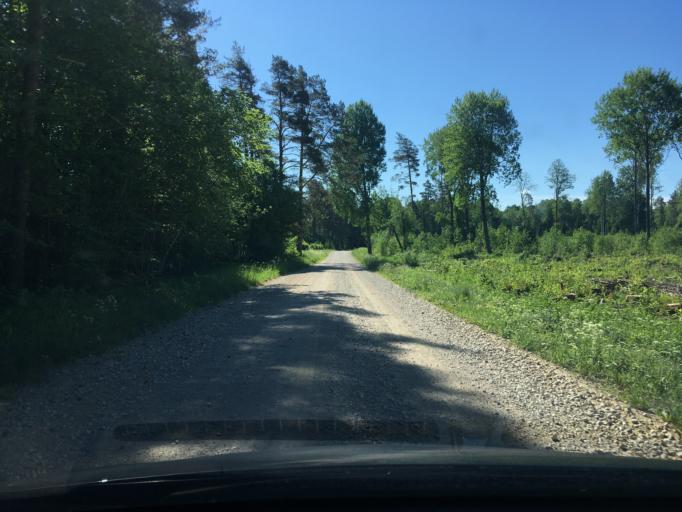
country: EE
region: Laeaene
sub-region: Lihula vald
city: Lihula
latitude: 58.6454
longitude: 23.7839
